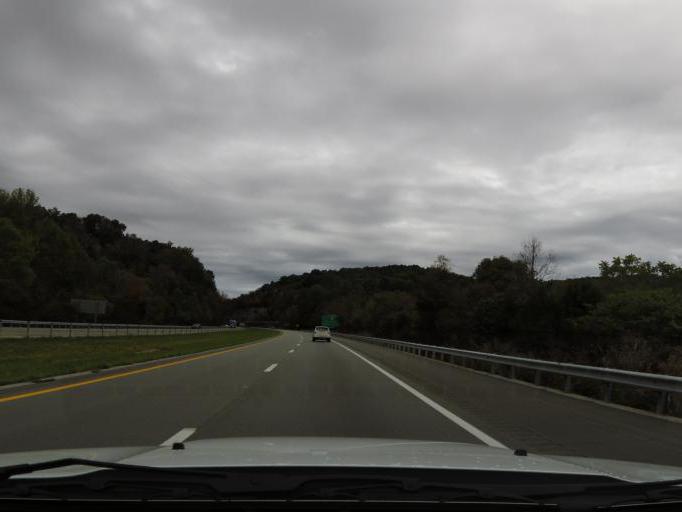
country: US
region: Kentucky
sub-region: Rockcastle County
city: Mount Vernon
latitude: 37.3618
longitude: -84.3087
